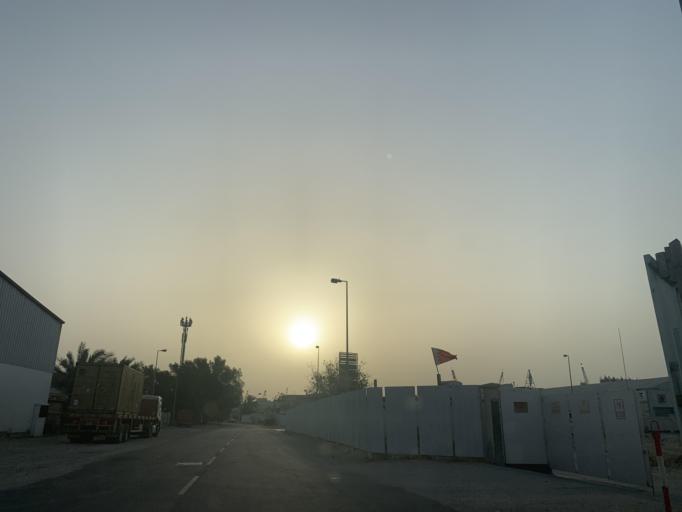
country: BH
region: Manama
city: Manama
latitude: 26.1972
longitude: 50.5931
